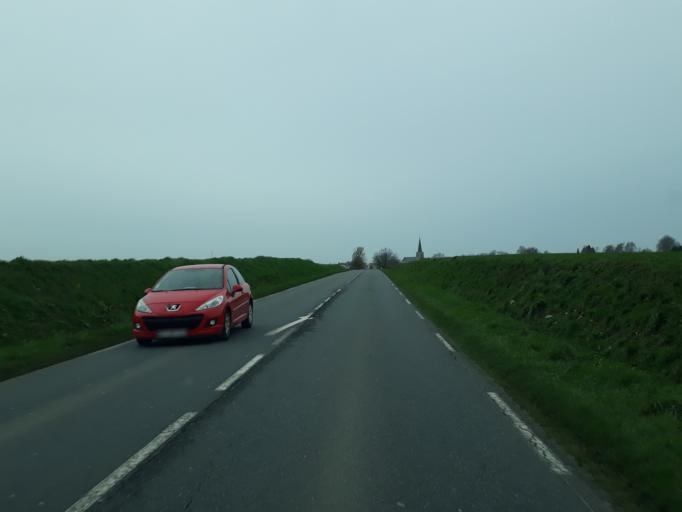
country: FR
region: Haute-Normandie
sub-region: Departement de la Seine-Maritime
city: Beuzeville-la-Grenier
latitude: 49.5869
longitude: 0.4366
